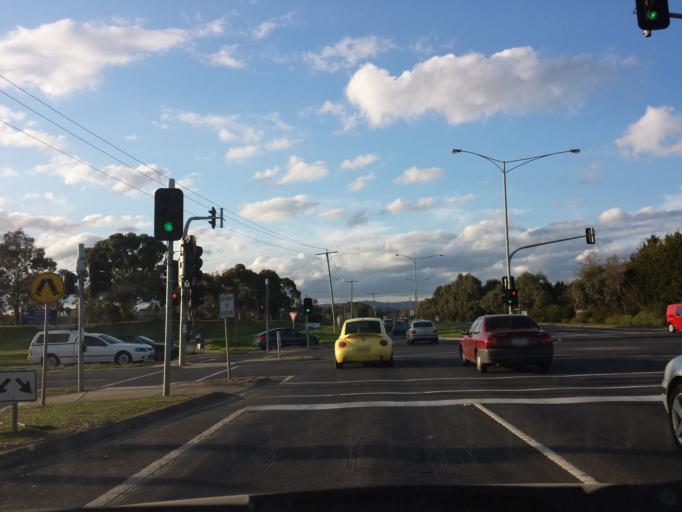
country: AU
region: Victoria
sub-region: Casey
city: Narre Warren North
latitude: -37.9968
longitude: 145.3126
